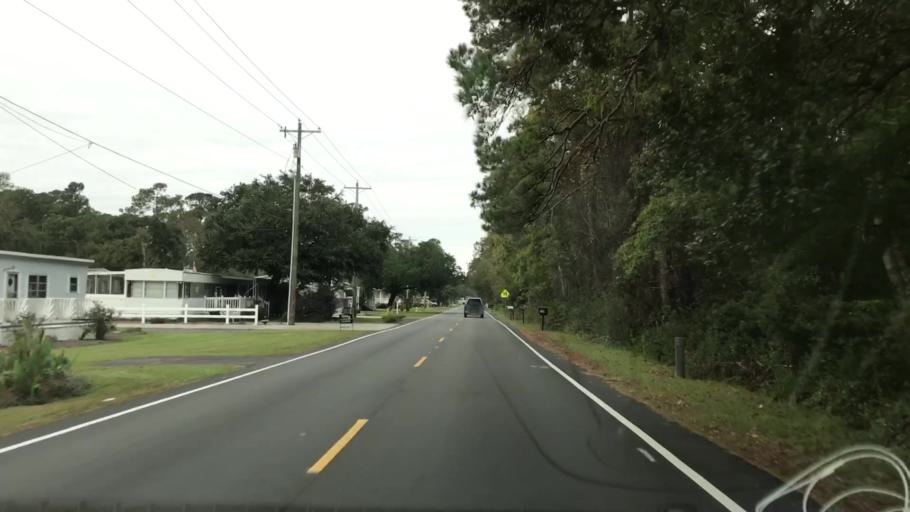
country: US
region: South Carolina
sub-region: Horry County
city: Garden City
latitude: 33.5867
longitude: -79.0019
